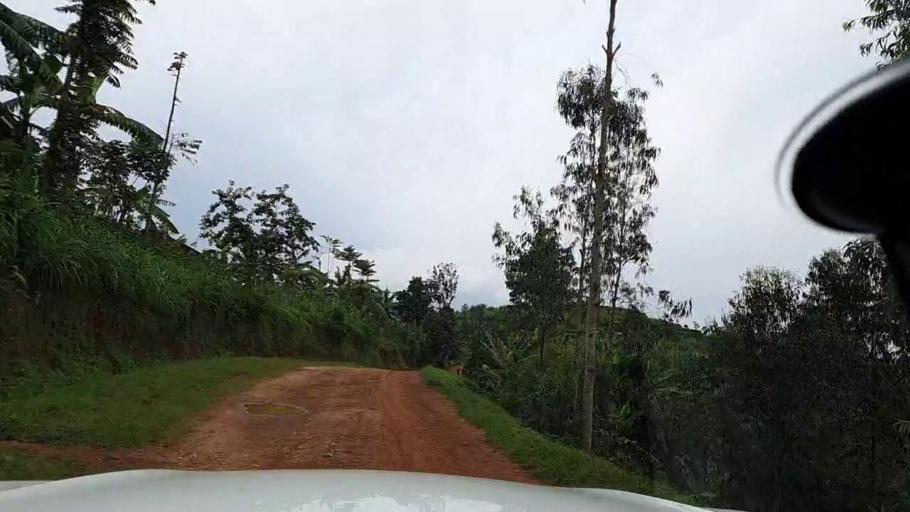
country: RW
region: Southern Province
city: Gitarama
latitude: -2.0871
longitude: 29.6357
